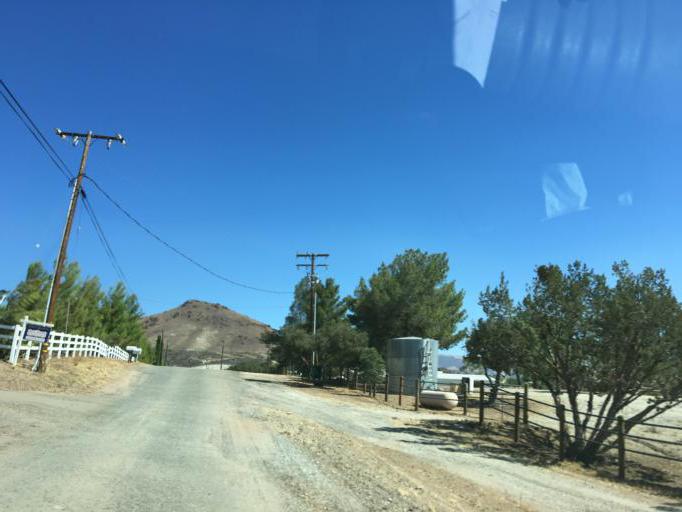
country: US
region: California
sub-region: Los Angeles County
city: Agua Dulce
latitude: 34.4772
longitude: -118.3439
